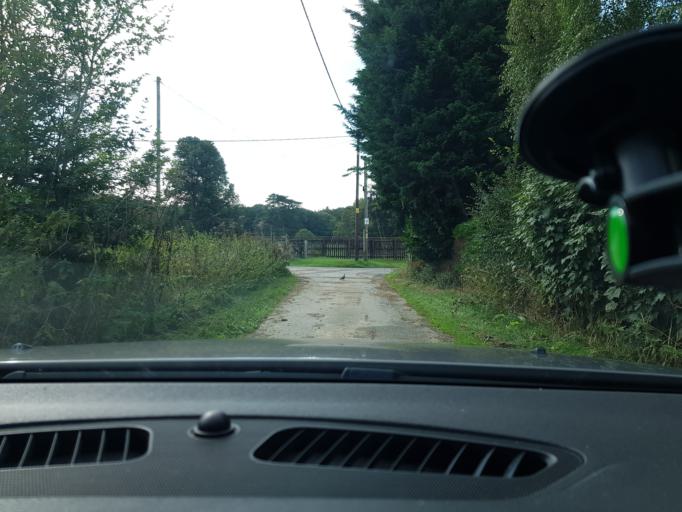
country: GB
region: England
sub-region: West Berkshire
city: Kintbury
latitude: 51.3972
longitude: -1.4829
